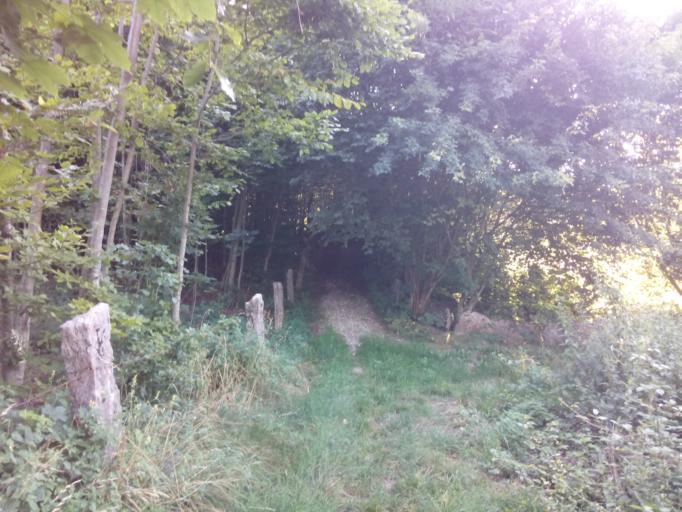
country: IT
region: Veneto
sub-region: Provincia di Vicenza
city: Conco
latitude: 45.8096
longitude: 11.6105
